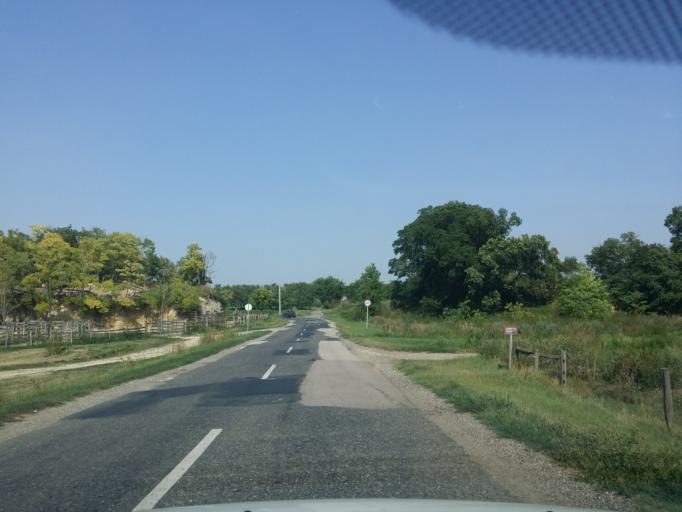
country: HU
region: Fejer
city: Sarbogard
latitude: 46.9201
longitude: 18.6757
